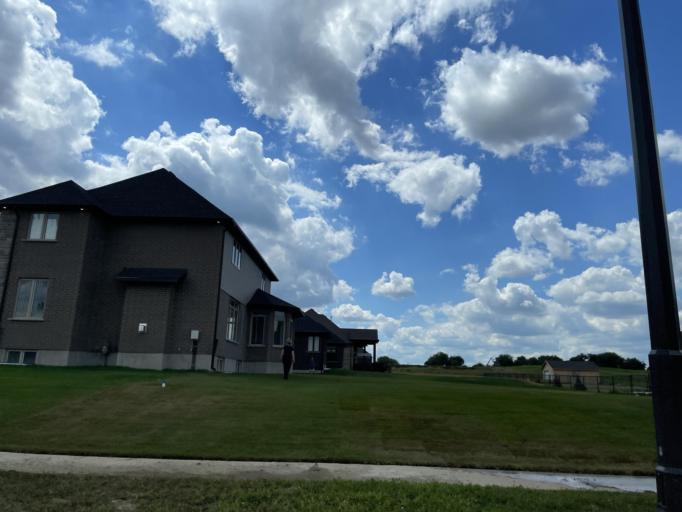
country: CA
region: Ontario
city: Waterloo
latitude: 43.5374
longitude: -80.3989
